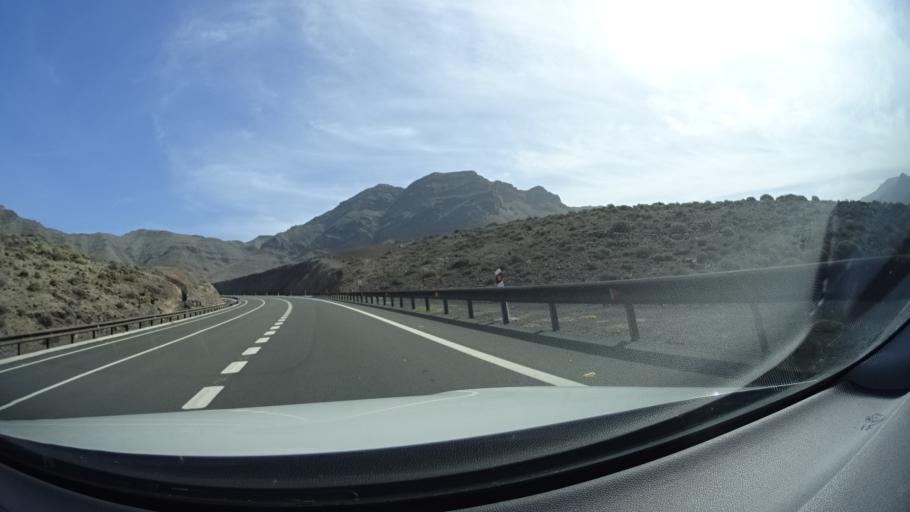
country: ES
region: Canary Islands
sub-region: Provincia de Las Palmas
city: San Nicolas
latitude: 28.0127
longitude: -15.7756
